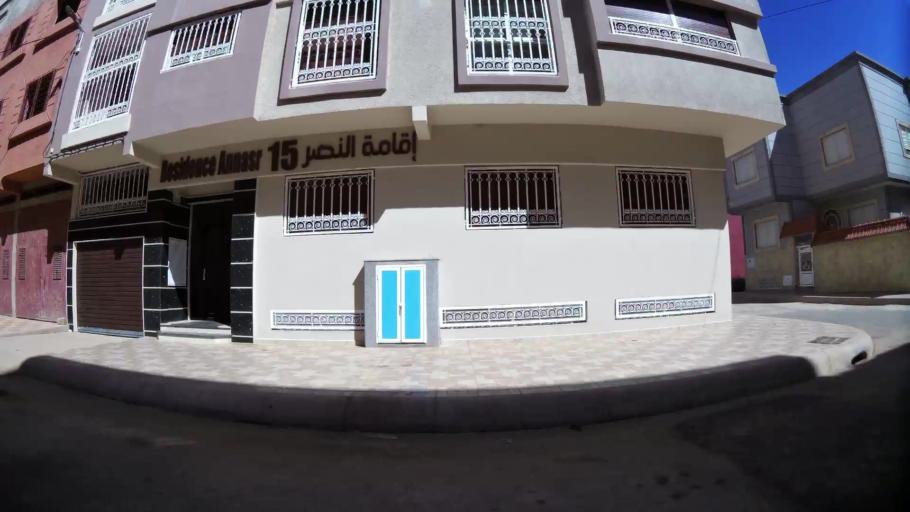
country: MA
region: Oriental
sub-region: Berkane-Taourirt
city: Berkane
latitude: 34.9376
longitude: -2.3232
